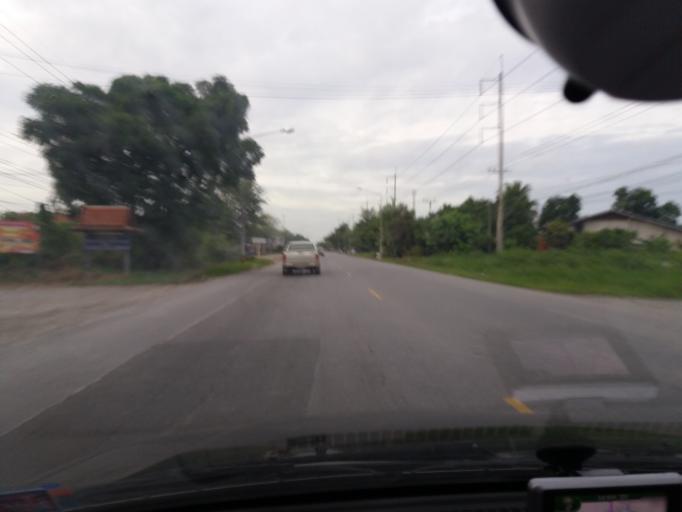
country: TH
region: Suphan Buri
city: U Thong
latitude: 14.4984
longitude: 99.9197
